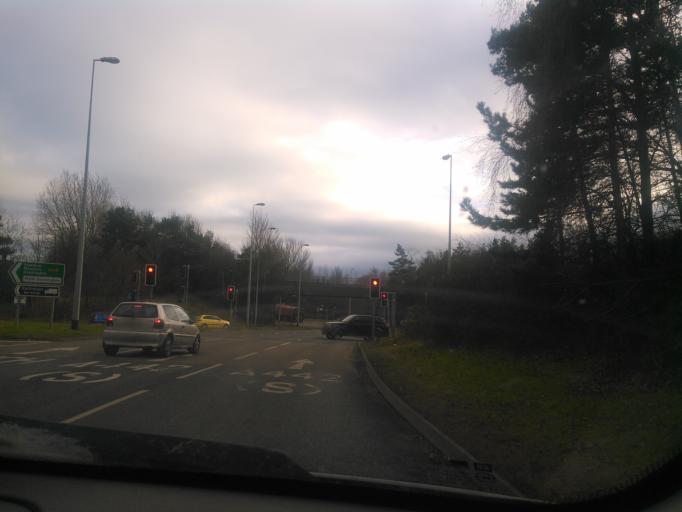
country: GB
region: England
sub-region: Shropshire
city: Hadley
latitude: 52.7114
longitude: -2.4699
